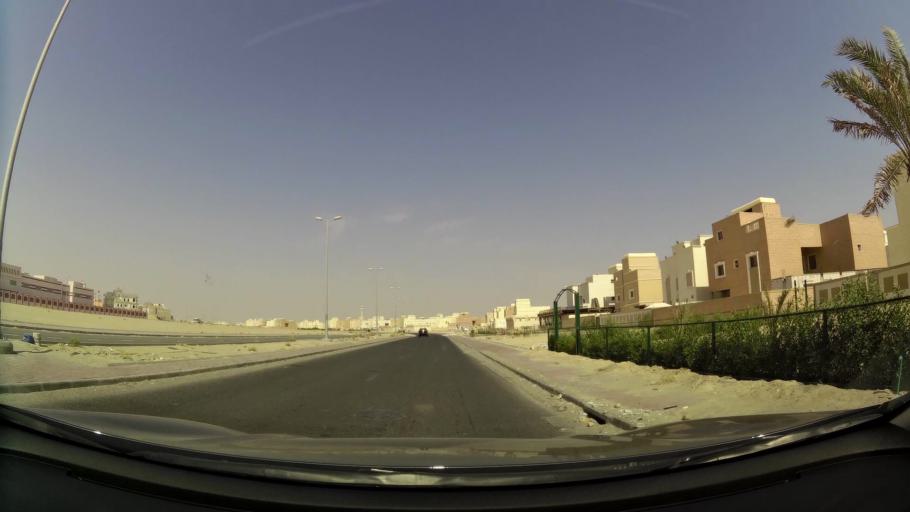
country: KW
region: Al Ahmadi
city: Al Wafrah
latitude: 28.7933
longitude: 48.0660
